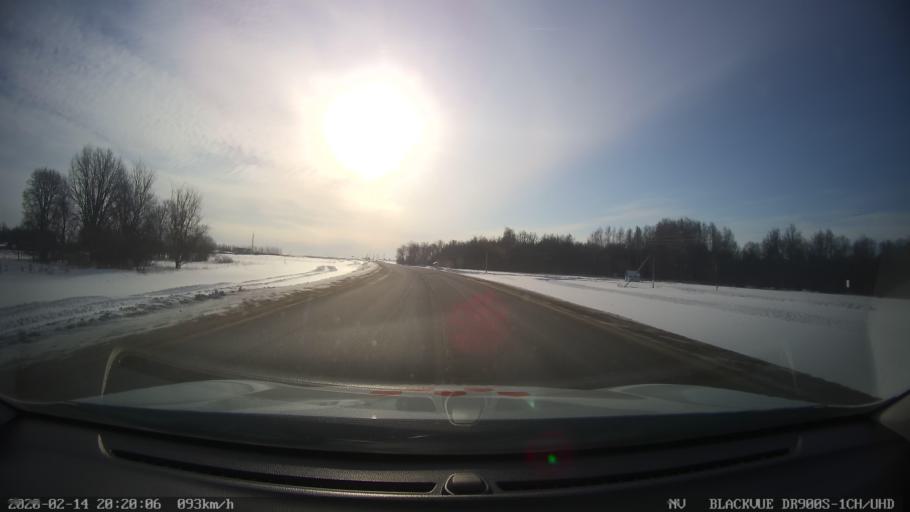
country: RU
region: Tatarstan
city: Verkhniy Uslon
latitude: 55.5609
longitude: 48.9020
